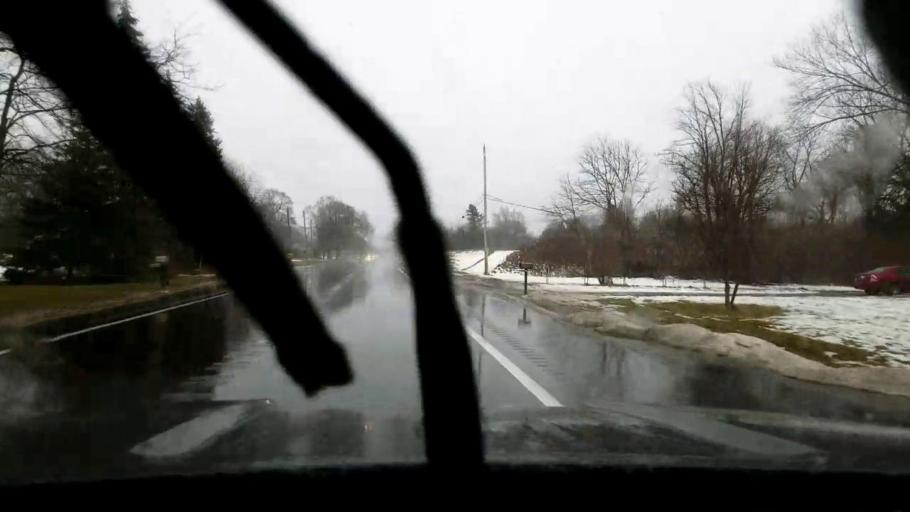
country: US
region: Michigan
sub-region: Jackson County
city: Michigan Center
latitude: 42.1919
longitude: -84.3194
